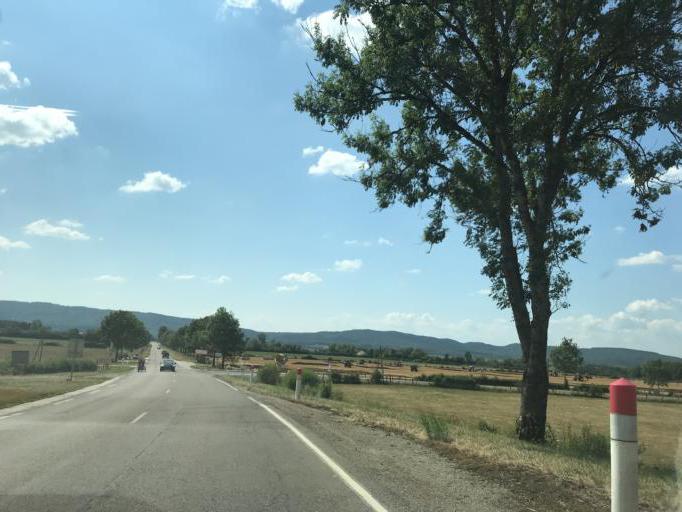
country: FR
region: Franche-Comte
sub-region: Departement du Jura
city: Clairvaux-les-Lacs
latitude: 46.5893
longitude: 5.7317
